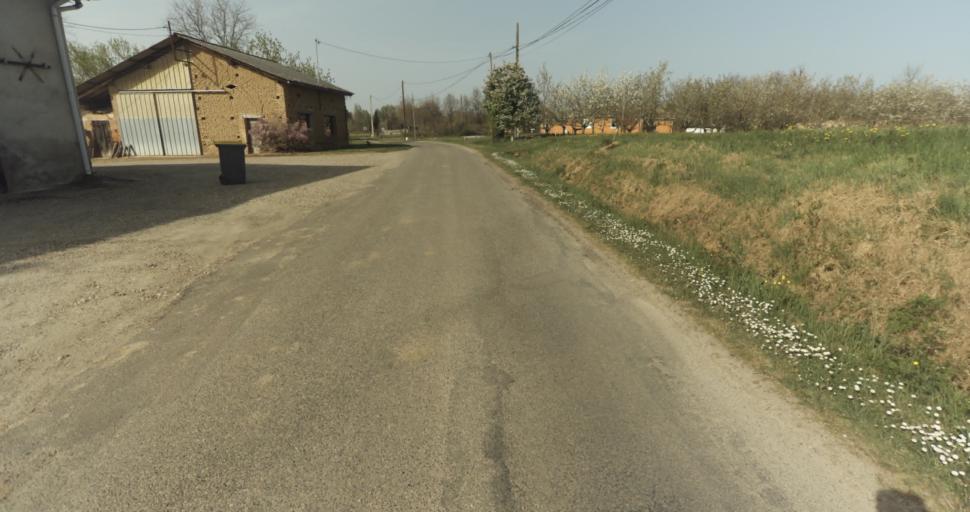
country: FR
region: Midi-Pyrenees
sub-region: Departement du Tarn-et-Garonne
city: Moissac
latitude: 44.1233
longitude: 1.1633
